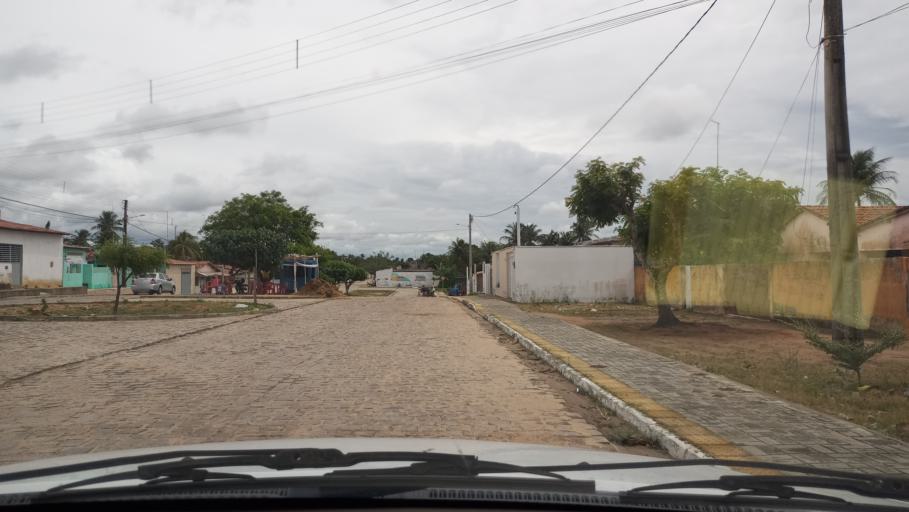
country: BR
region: Rio Grande do Norte
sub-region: Poco Branco
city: Poco Branco
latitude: -5.6186
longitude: -35.6587
